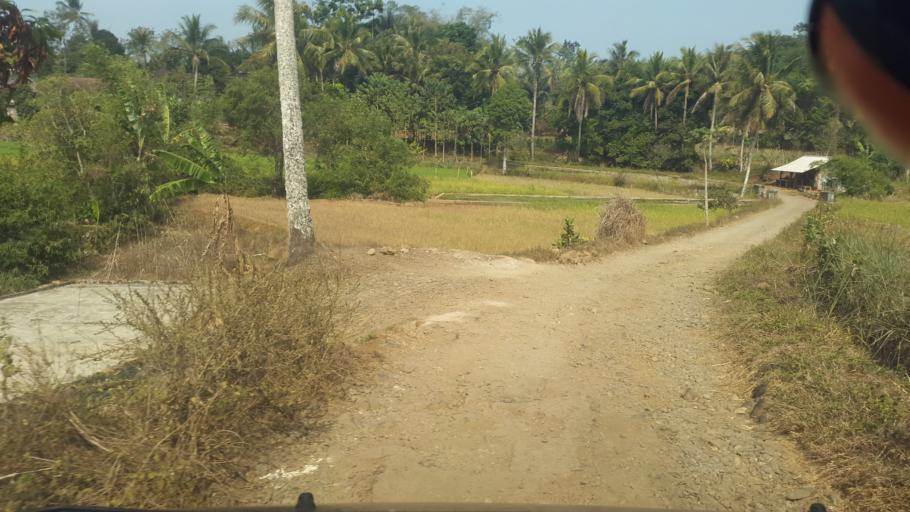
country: ID
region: West Java
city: Nangerang
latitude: -7.1113
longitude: 106.7971
